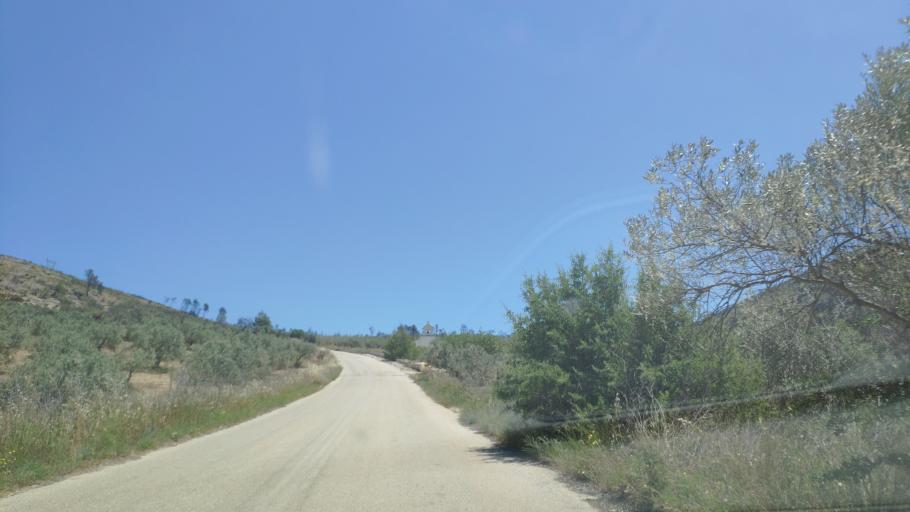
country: GR
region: Peloponnese
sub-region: Nomos Korinthias
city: Athikia
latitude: 37.8356
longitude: 22.9360
